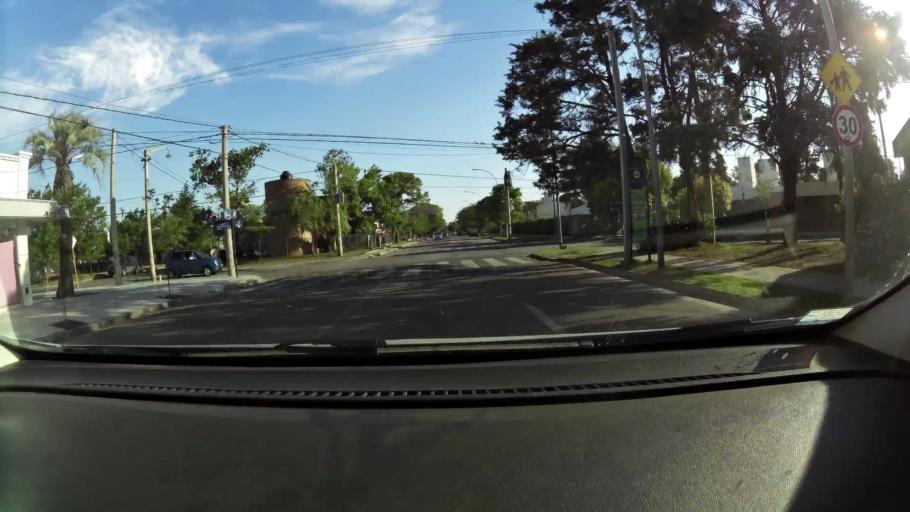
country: AR
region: Cordoba
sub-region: Departamento de Capital
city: Cordoba
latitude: -31.3684
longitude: -64.2264
